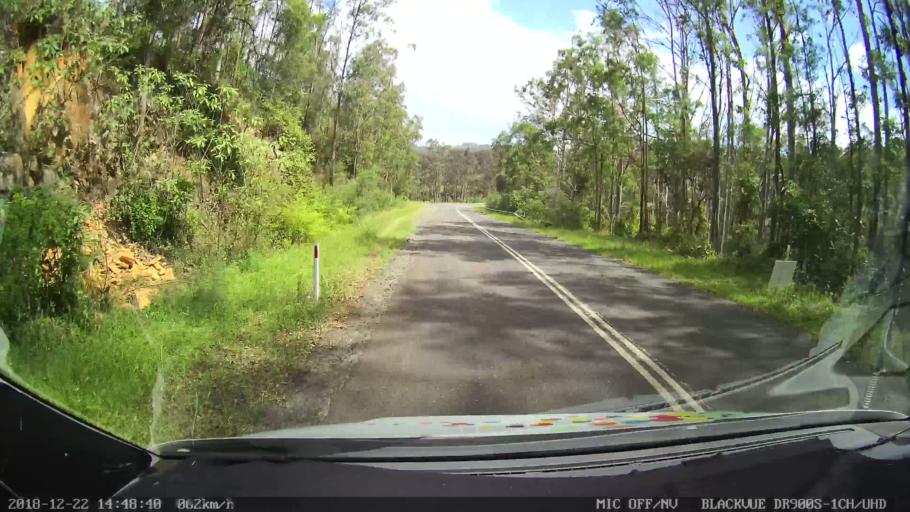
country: AU
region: New South Wales
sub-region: Bellingen
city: Dorrigo
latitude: -30.1823
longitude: 152.5516
